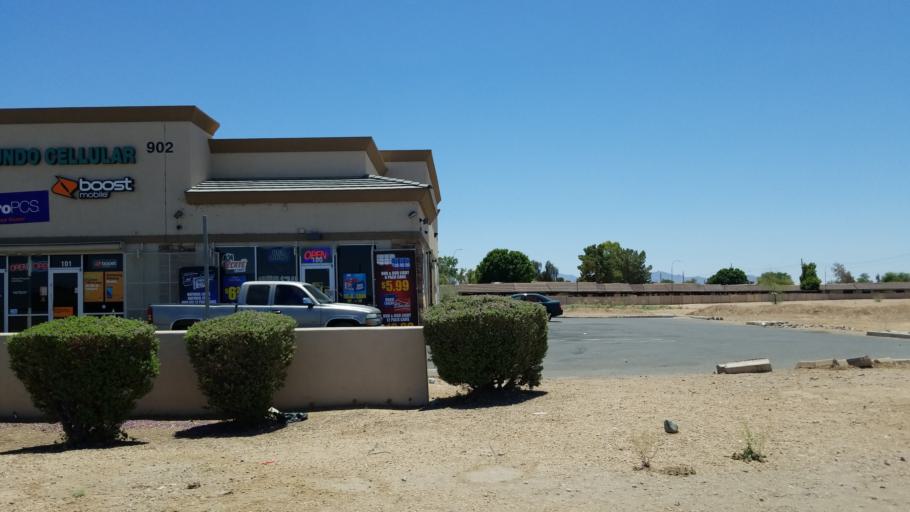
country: US
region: Arizona
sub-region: Maricopa County
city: Tolleson
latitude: 33.5087
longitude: -112.2537
